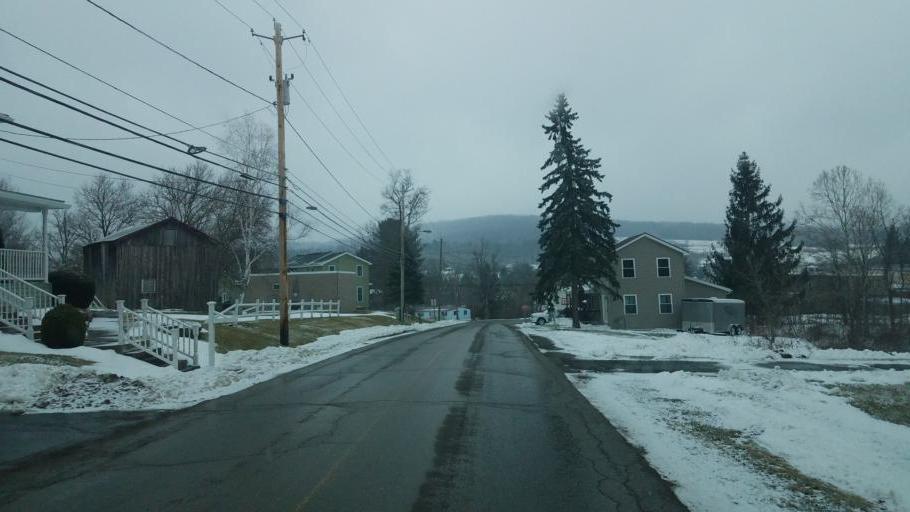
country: US
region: Pennsylvania
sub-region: Tioga County
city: Elkland
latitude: 42.0816
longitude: -77.4090
